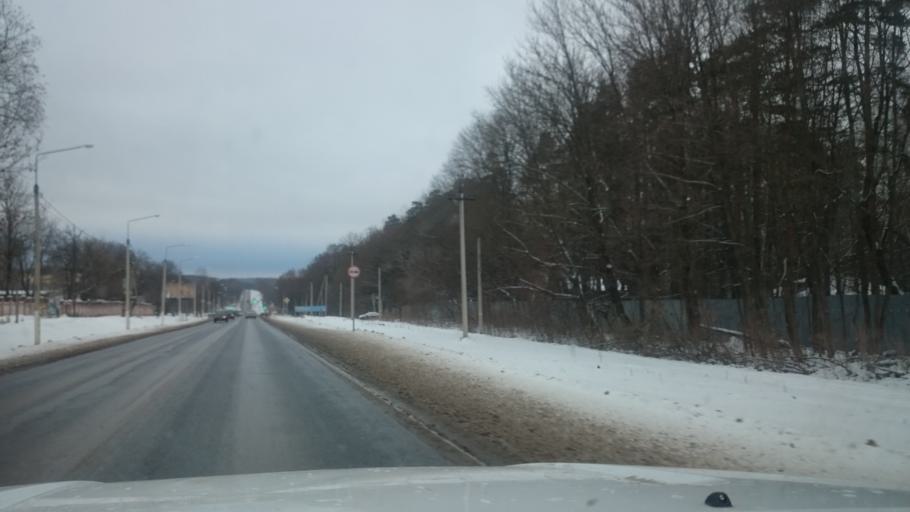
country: RU
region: Tula
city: Kosaya Gora
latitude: 54.0845
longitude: 37.5449
